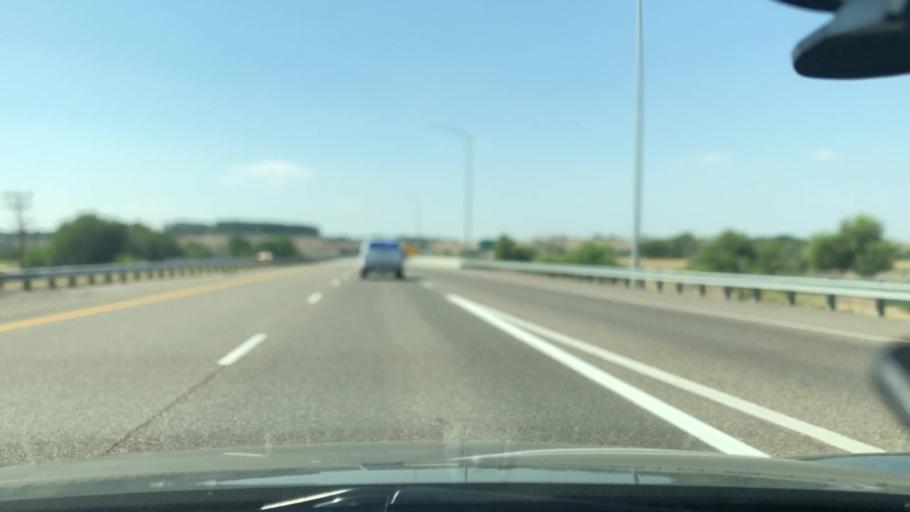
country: US
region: Oregon
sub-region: Malheur County
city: Ontario
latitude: 44.0523
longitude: -116.9809
